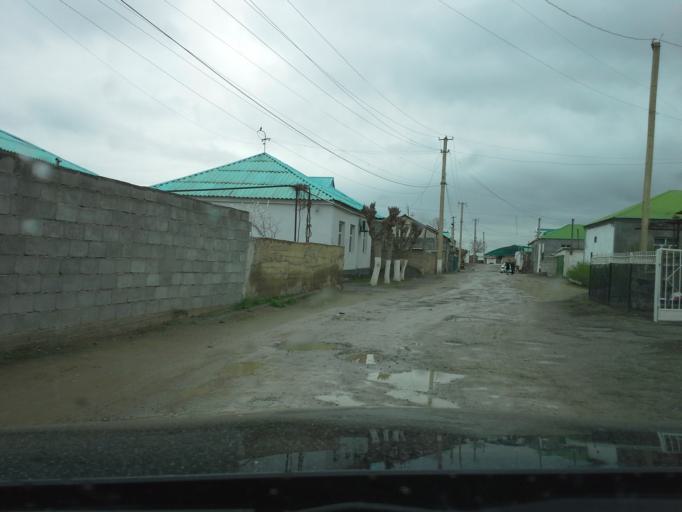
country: TM
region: Ahal
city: Abadan
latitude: 37.9525
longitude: 58.2050
